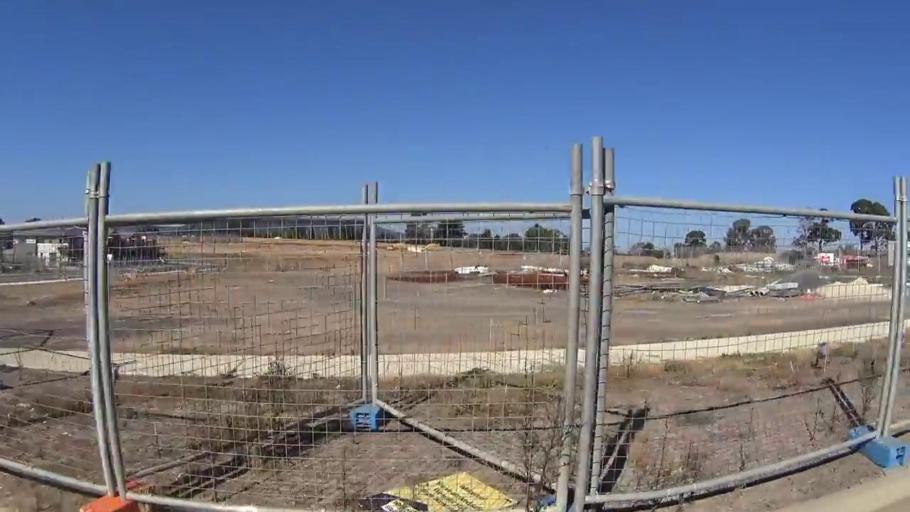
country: AU
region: Victoria
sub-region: Knox
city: Knoxfield
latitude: -37.8864
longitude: 145.2362
